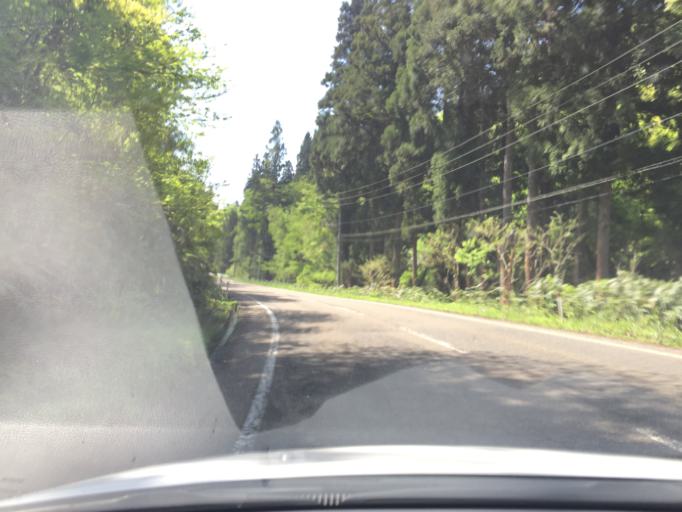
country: JP
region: Niigata
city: Tochio-honcho
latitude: 37.5338
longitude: 139.0923
